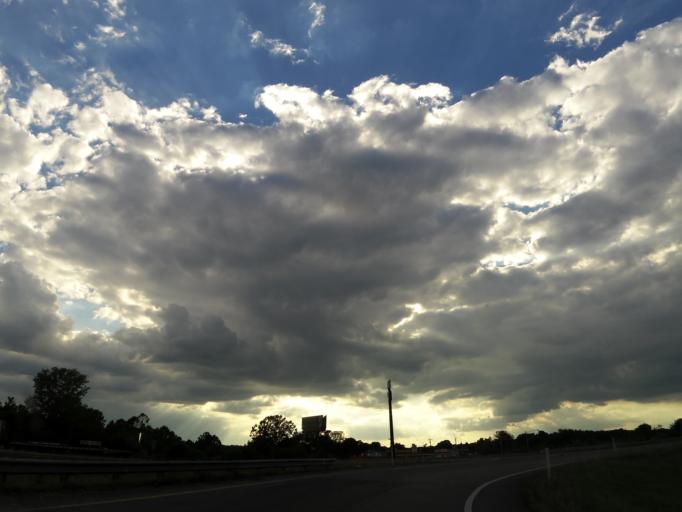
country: US
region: Tennessee
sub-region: Maury County
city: Spring Hill
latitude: 35.6417
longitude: -86.8930
